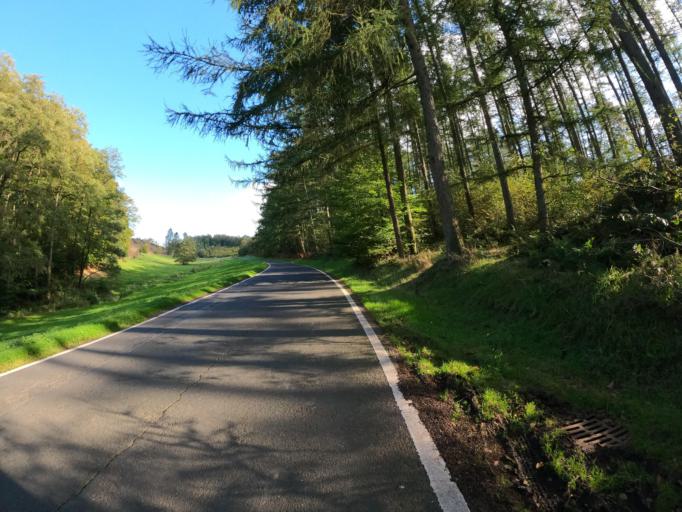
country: DE
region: North Rhine-Westphalia
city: Radevormwald
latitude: 51.2356
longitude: 7.3215
